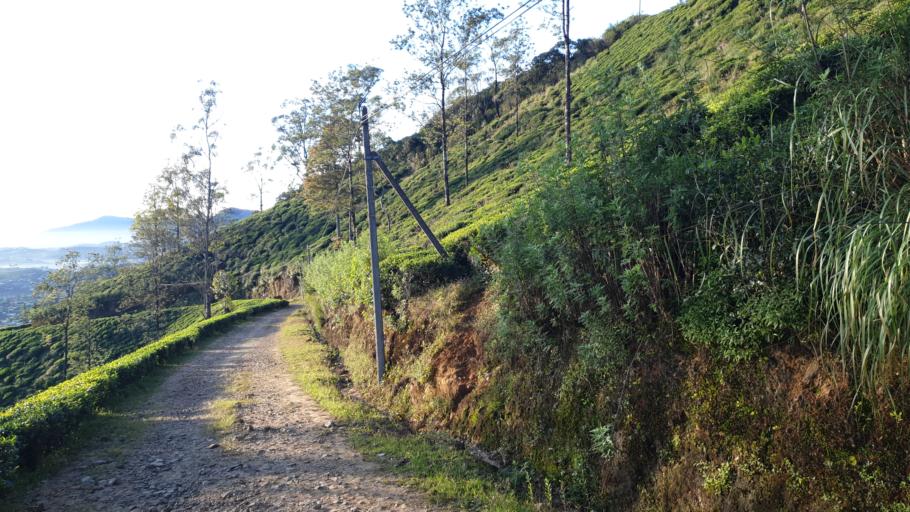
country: LK
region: Central
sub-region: Nuwara Eliya District
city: Nuwara Eliya
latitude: 6.9582
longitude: 80.7636
